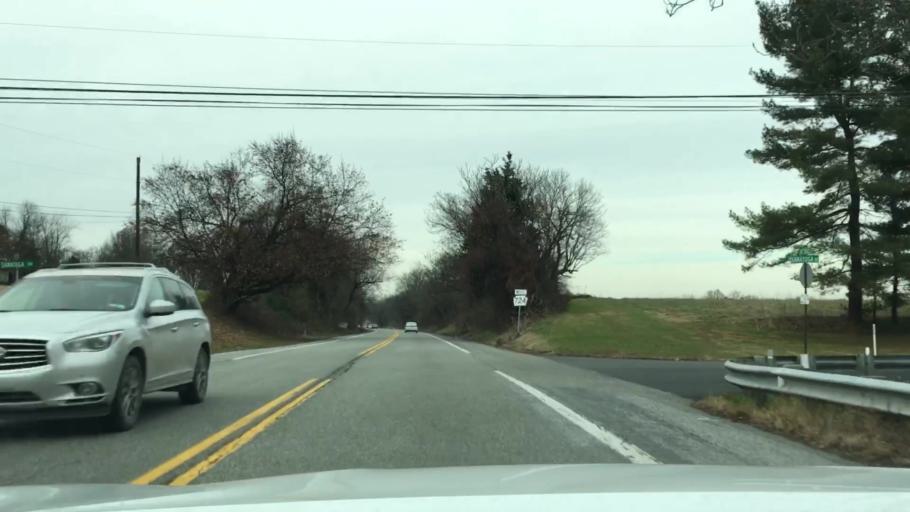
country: US
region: Pennsylvania
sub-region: Montgomery County
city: Sanatoga
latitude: 40.2129
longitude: -75.6000
